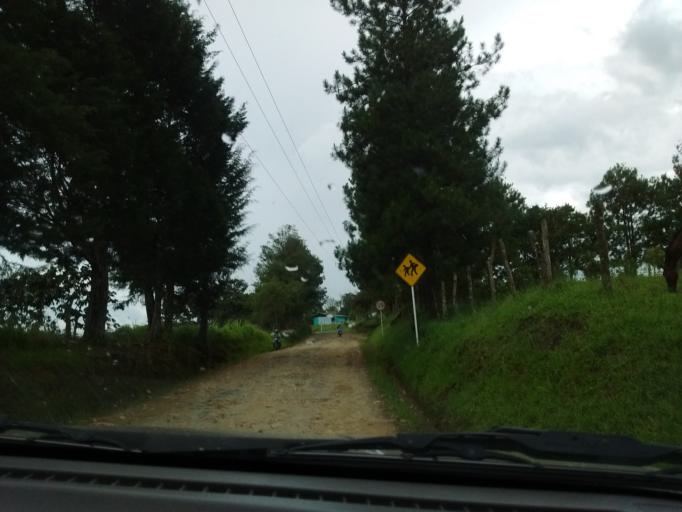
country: CO
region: Cauca
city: Cajibio
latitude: 2.5839
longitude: -76.6747
